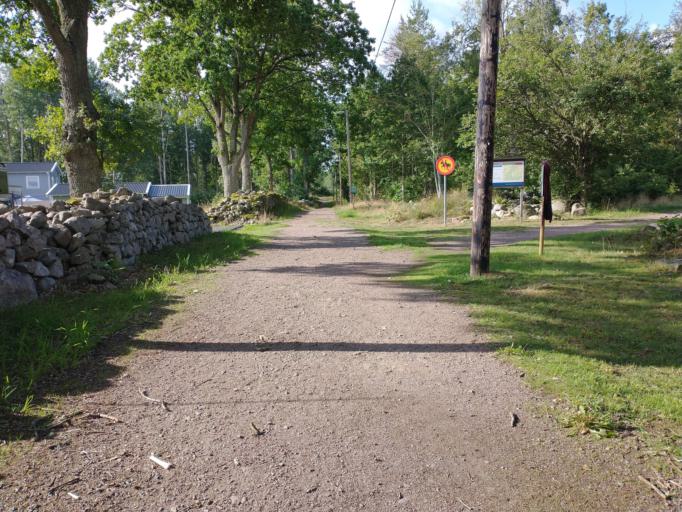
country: SE
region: Kalmar
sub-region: Kalmar Kommun
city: Lindsdal
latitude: 56.7791
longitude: 16.2996
